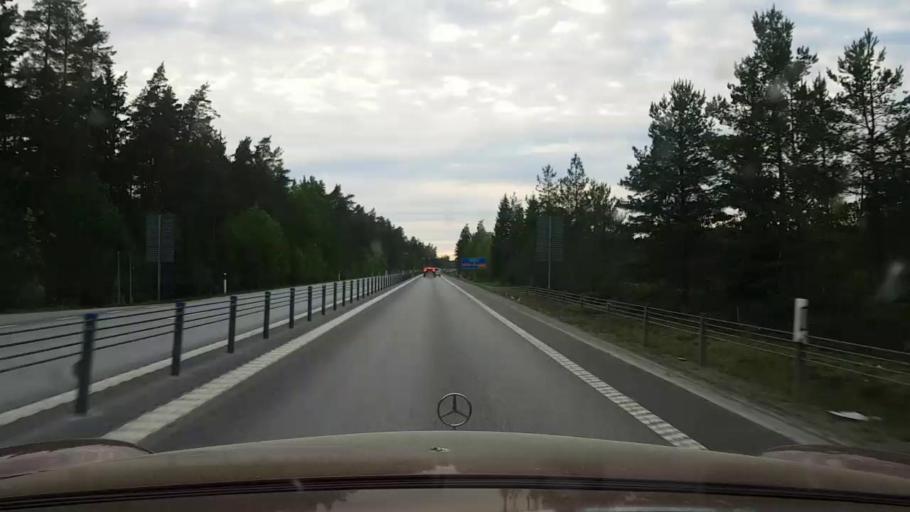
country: SE
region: OErebro
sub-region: Askersunds Kommun
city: Asbro
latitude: 59.0113
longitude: 15.0404
